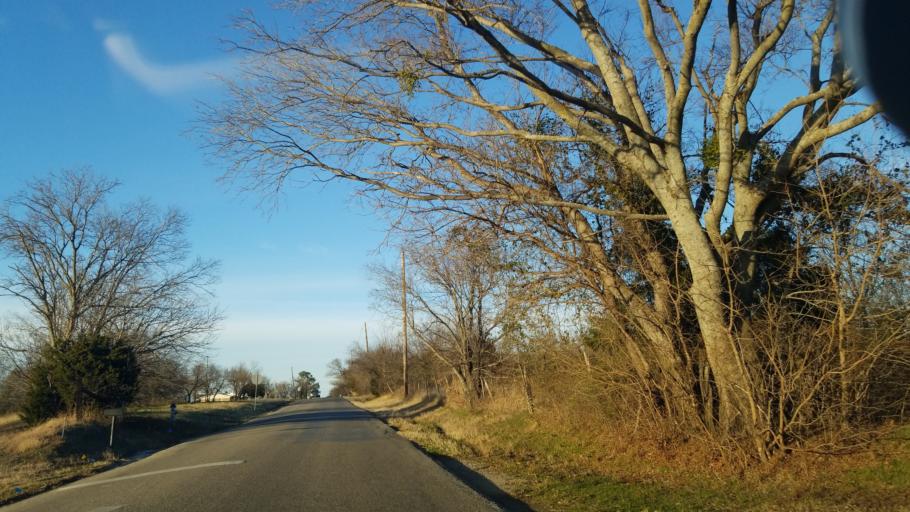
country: US
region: Texas
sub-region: Denton County
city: Denton
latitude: 33.1943
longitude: -97.1616
